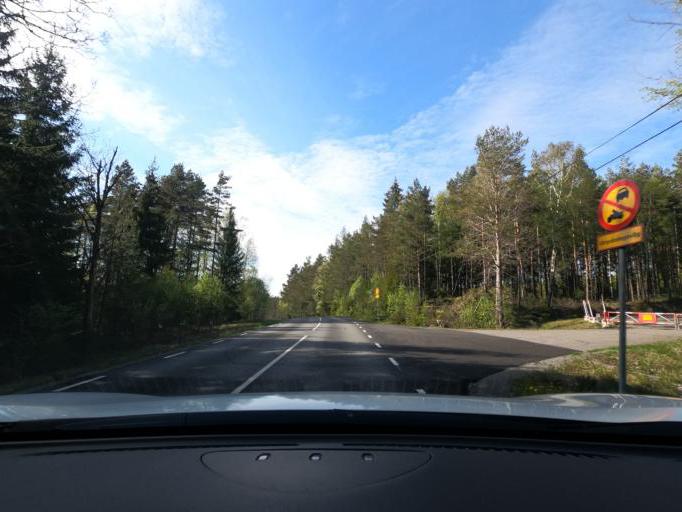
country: SE
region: Vaestra Goetaland
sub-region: Harryda Kommun
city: Landvetter
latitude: 57.6380
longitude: 12.2579
